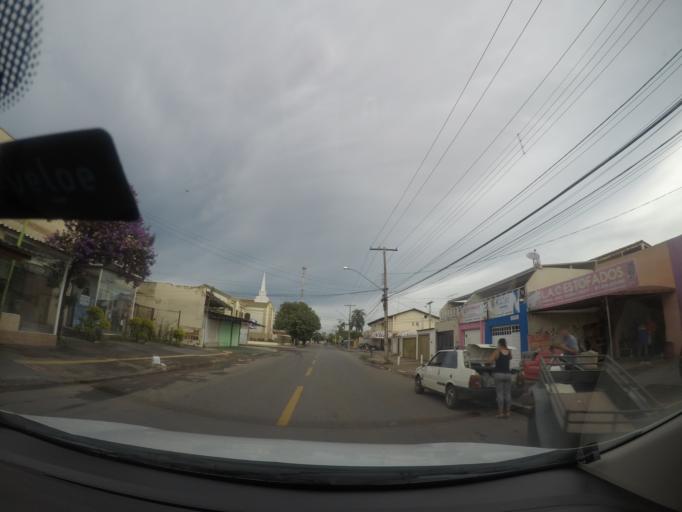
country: BR
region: Goias
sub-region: Goiania
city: Goiania
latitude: -16.7044
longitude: -49.3074
